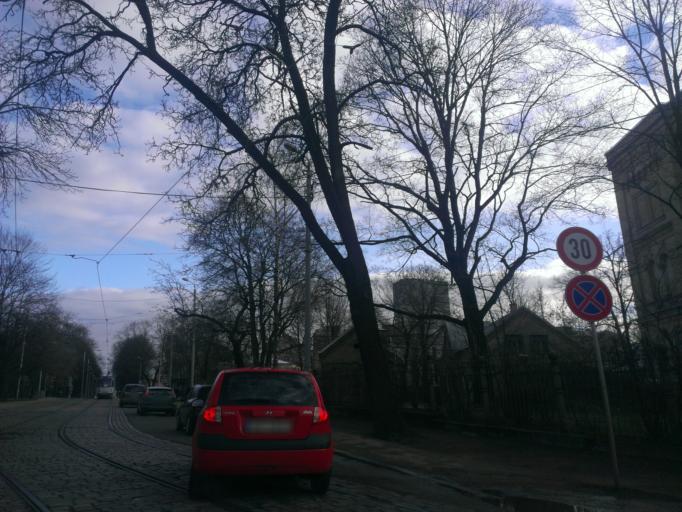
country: LV
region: Riga
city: Riga
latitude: 56.9584
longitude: 24.0999
